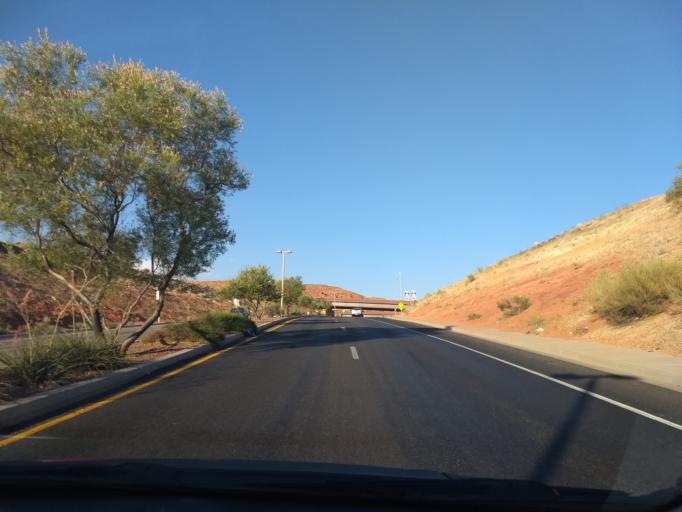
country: US
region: Utah
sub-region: Washington County
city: Saint George
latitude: 37.1336
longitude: -113.6055
